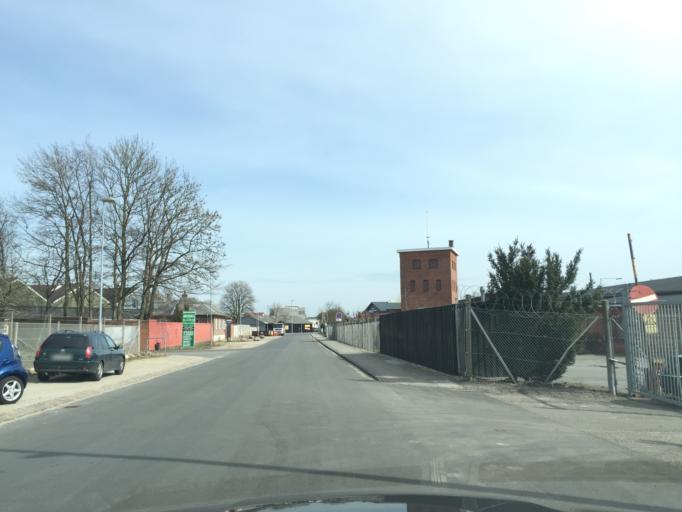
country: DK
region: South Denmark
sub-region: Odense Kommune
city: Odense
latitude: 55.3929
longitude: 10.3613
